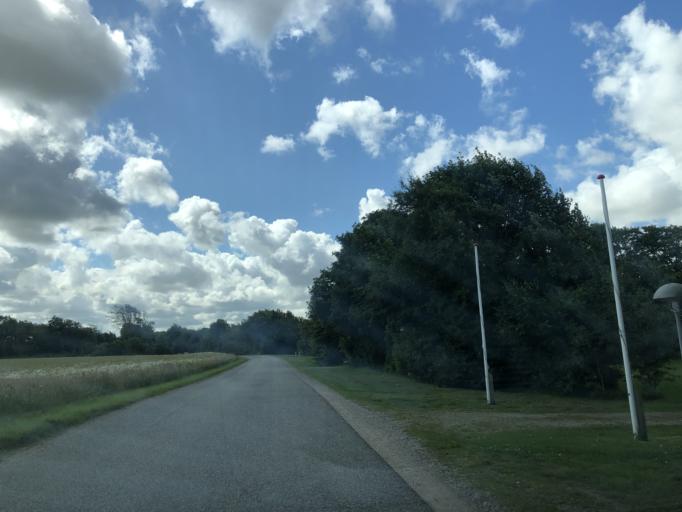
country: DK
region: Central Jutland
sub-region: Struer Kommune
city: Struer
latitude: 56.4610
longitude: 8.5225
